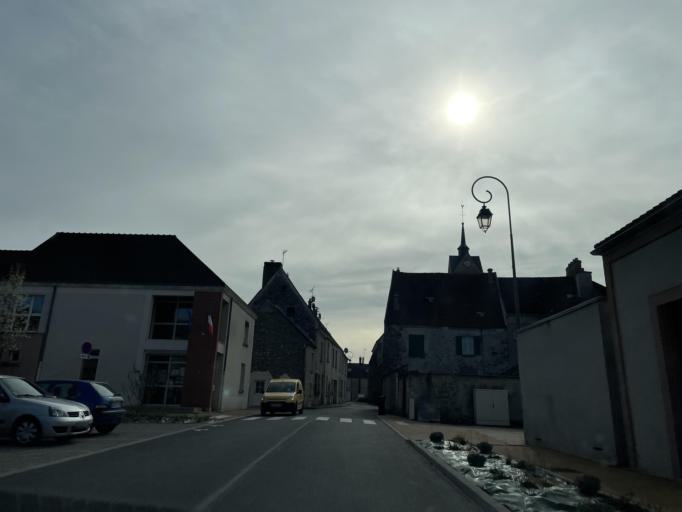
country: FR
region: Ile-de-France
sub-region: Departement de Seine-et-Marne
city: Chailly-en-Brie
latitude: 48.7408
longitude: 3.1283
